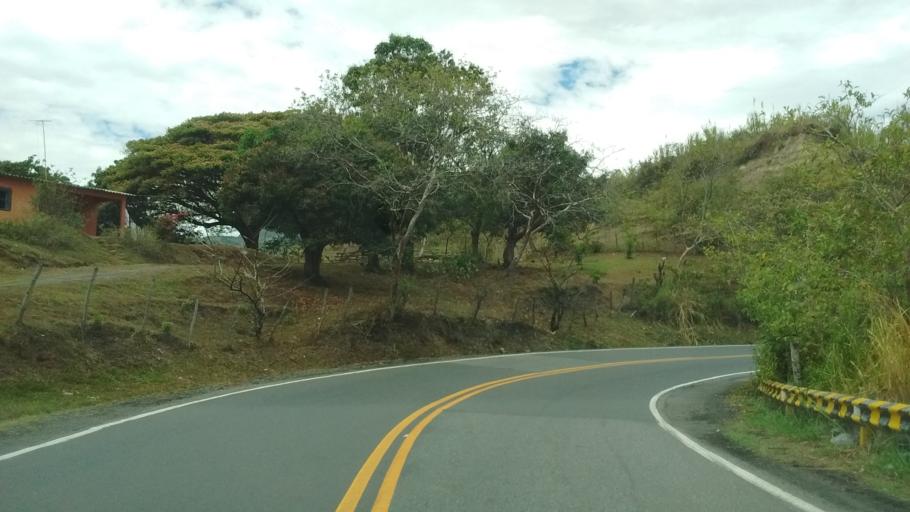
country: CO
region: Cauca
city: La Sierra
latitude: 2.2306
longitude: -76.7936
